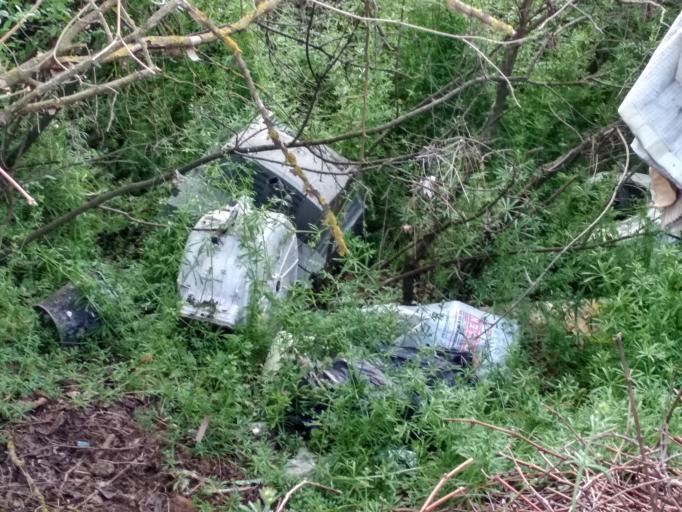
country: HU
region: Tolna
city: Bonyhad
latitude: 46.2749
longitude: 18.5456
